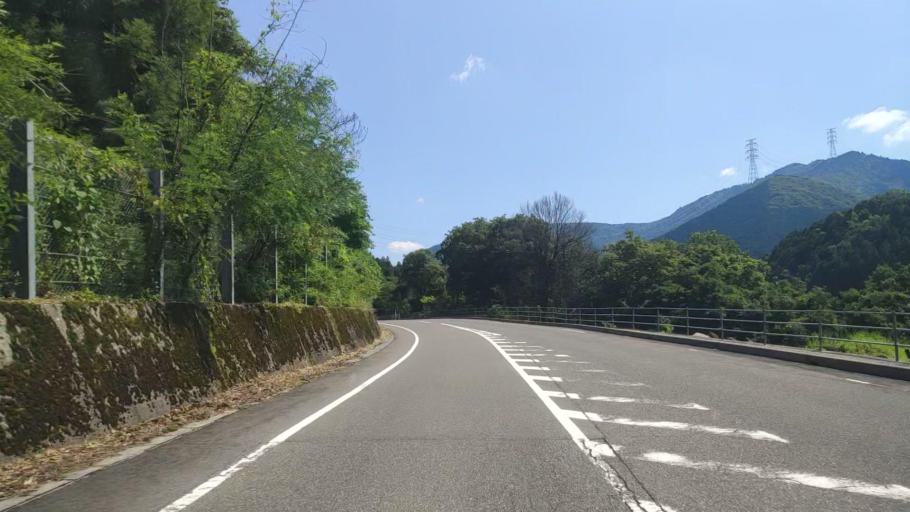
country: JP
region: Gifu
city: Godo
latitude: 35.5979
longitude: 136.6285
